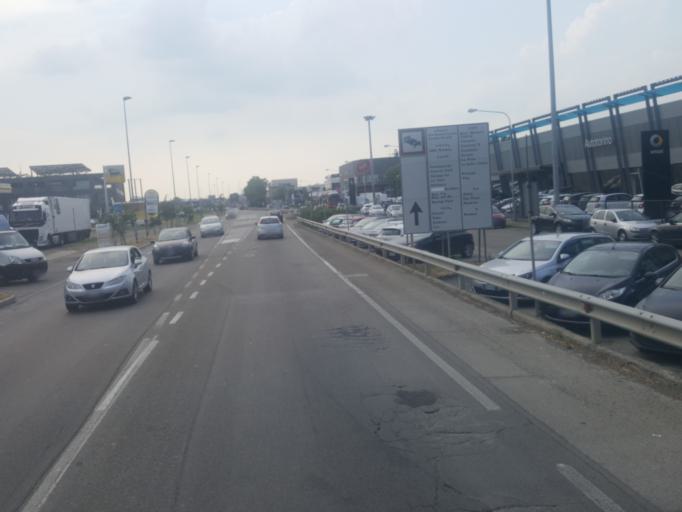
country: IT
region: Emilia-Romagna
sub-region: Provincia di Modena
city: San Damaso
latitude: 44.6311
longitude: 10.9629
